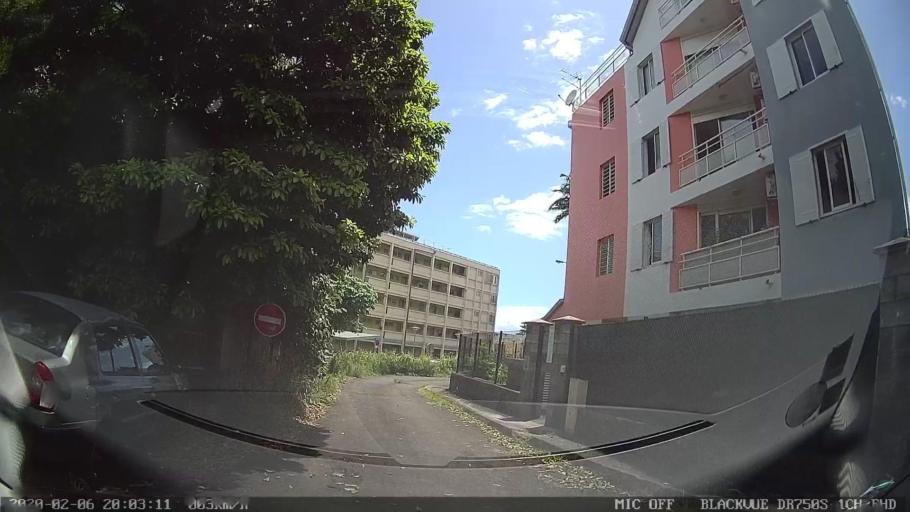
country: RE
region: Reunion
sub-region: Reunion
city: Saint-Denis
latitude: -20.8961
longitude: 55.4620
